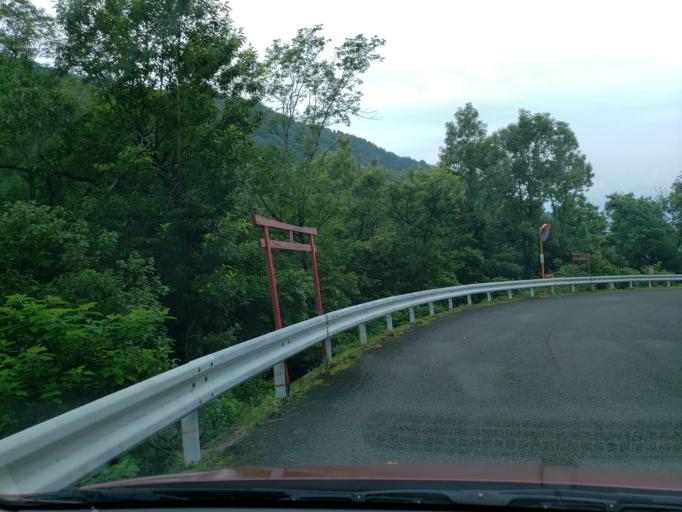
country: JP
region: Tokushima
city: Kamojimacho-jogejima
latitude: 34.1127
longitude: 134.3003
